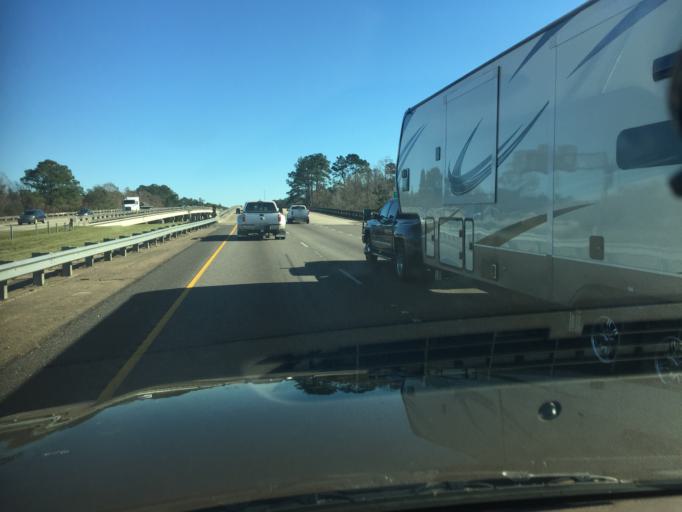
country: US
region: Louisiana
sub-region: Saint Tammany Parish
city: Covington
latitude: 30.4402
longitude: -90.1203
